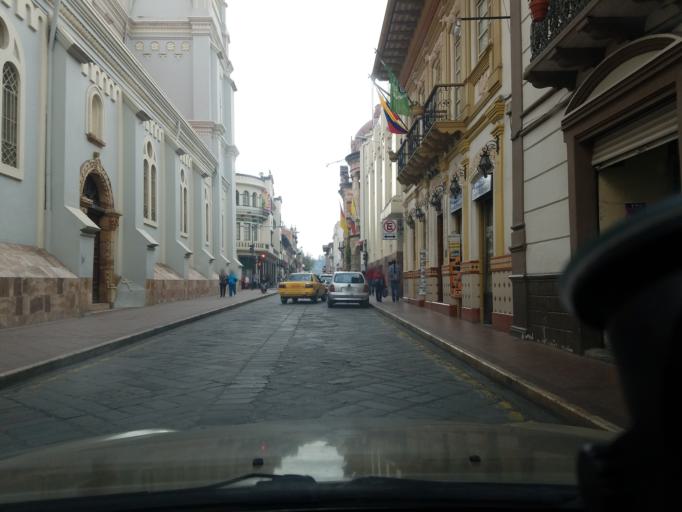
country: EC
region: Azuay
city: Cuenca
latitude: -2.8969
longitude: -79.0029
